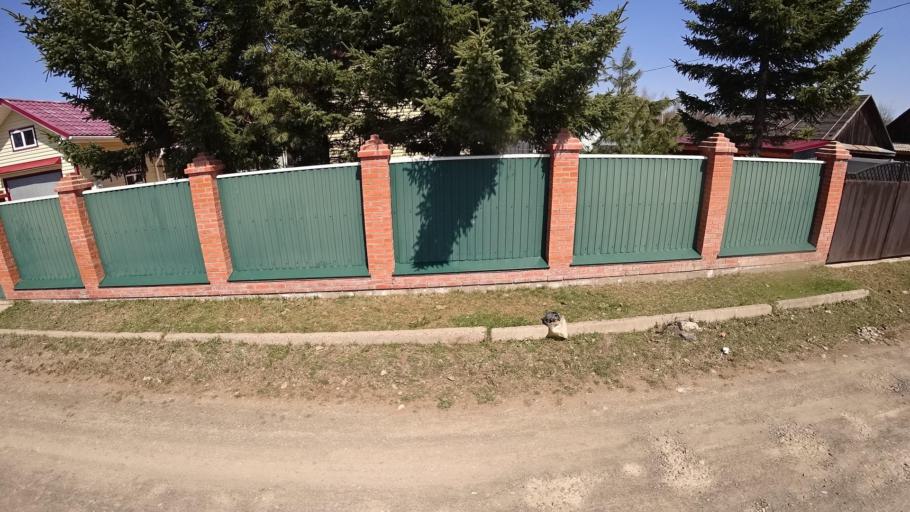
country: RU
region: Khabarovsk Krai
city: Khurba
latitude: 50.4138
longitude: 136.8650
